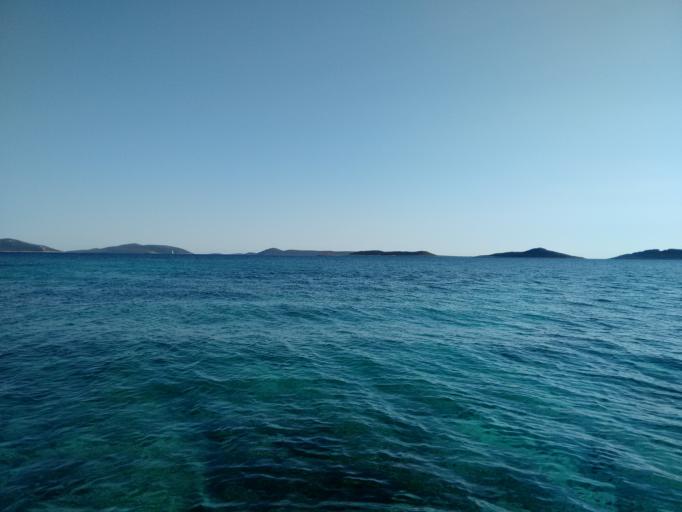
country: HR
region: Licko-Senjska
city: Novalja
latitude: 44.3487
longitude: 14.7177
